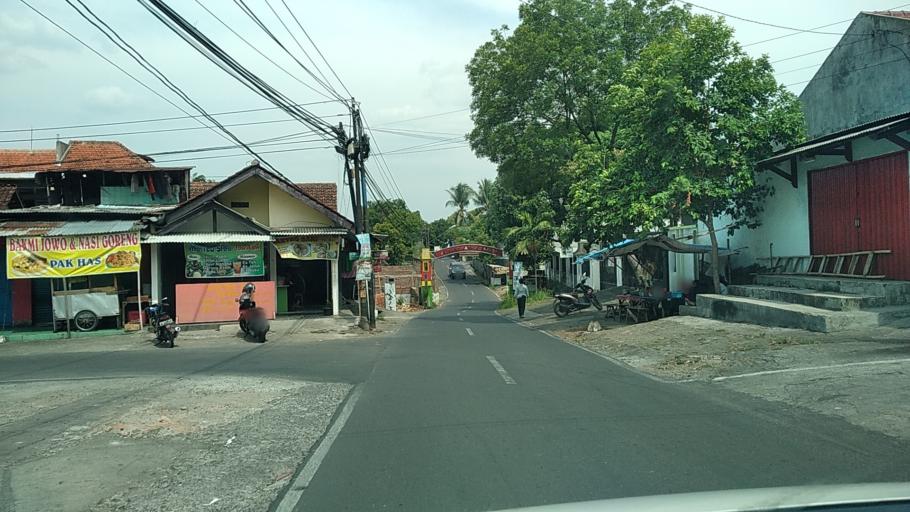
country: ID
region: Central Java
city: Semarang
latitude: -7.0342
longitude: 110.4267
